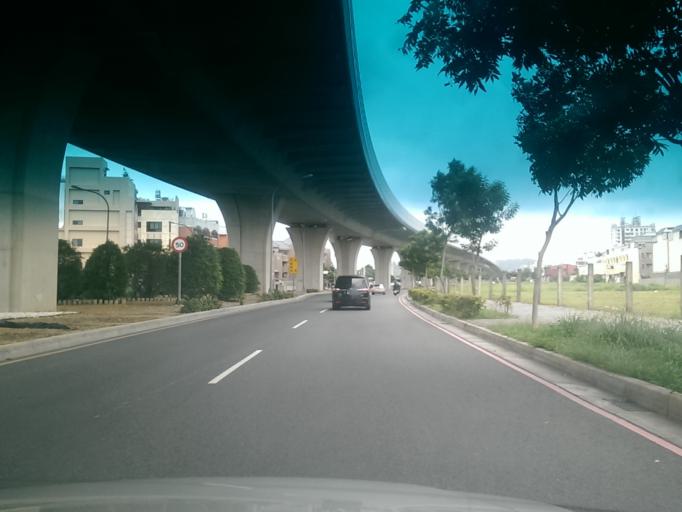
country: TW
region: Taiwan
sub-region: Taichung City
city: Taichung
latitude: 24.1426
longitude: 120.7112
